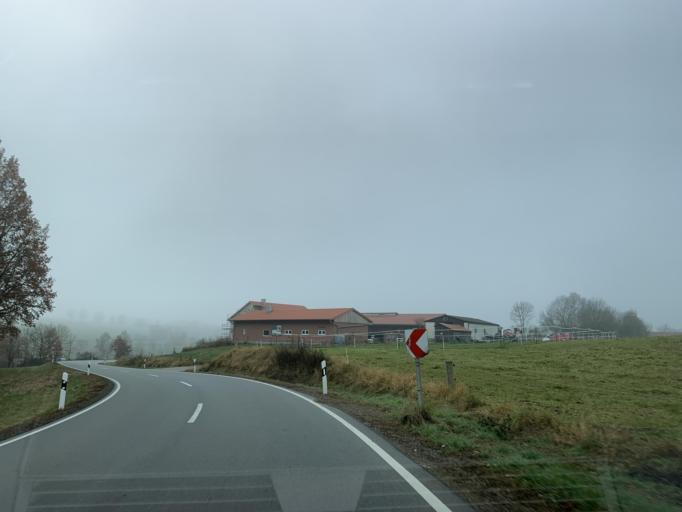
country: DE
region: Bavaria
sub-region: Upper Palatinate
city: Neunburg vorm Wald
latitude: 49.3514
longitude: 12.4049
